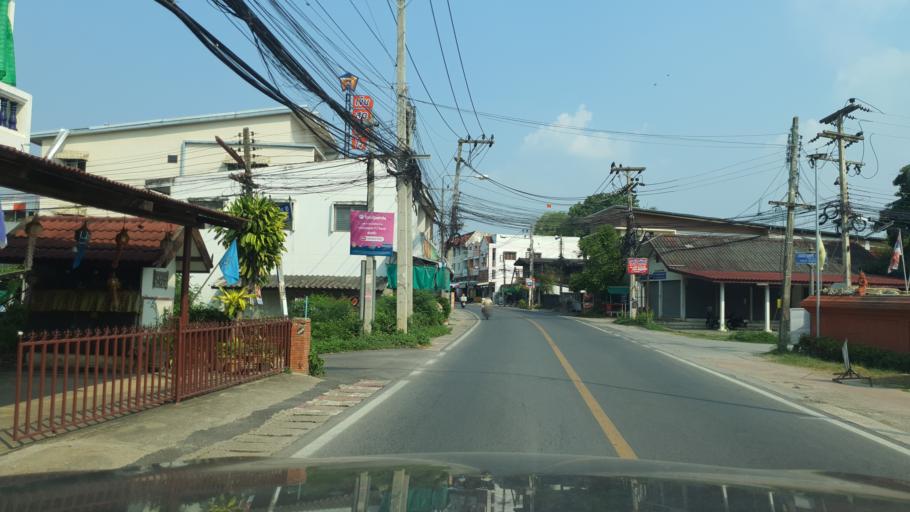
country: TH
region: Lamphun
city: Lamphun
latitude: 18.5819
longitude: 98.9967
